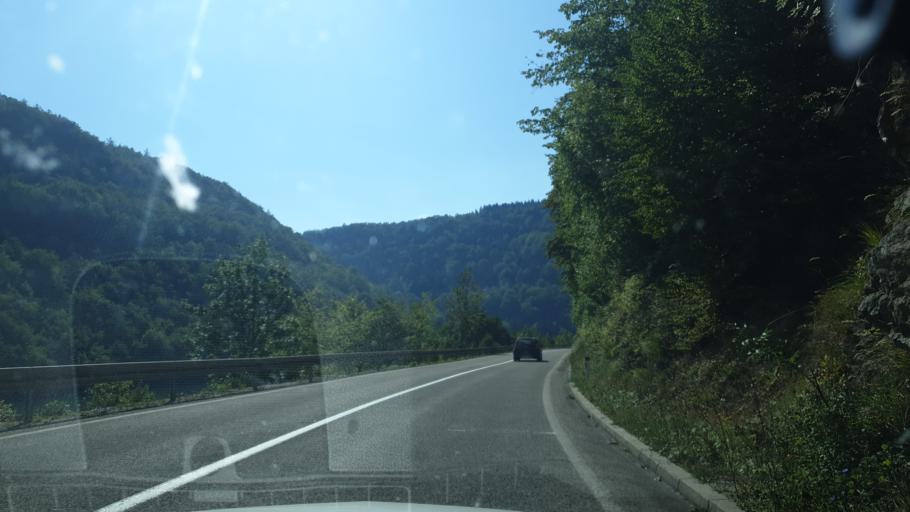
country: RS
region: Central Serbia
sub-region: Zlatiborski Okrug
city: Nova Varos
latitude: 43.5037
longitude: 19.8208
